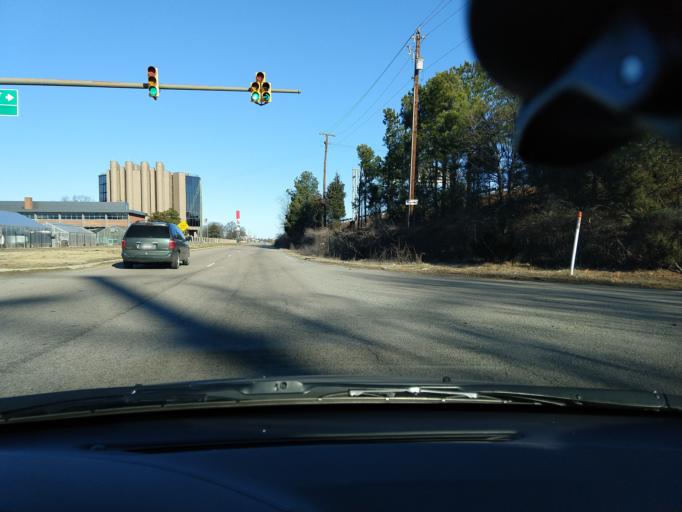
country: US
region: Virginia
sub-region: Chesterfield County
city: Bensley
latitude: 37.4682
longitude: -77.4283
